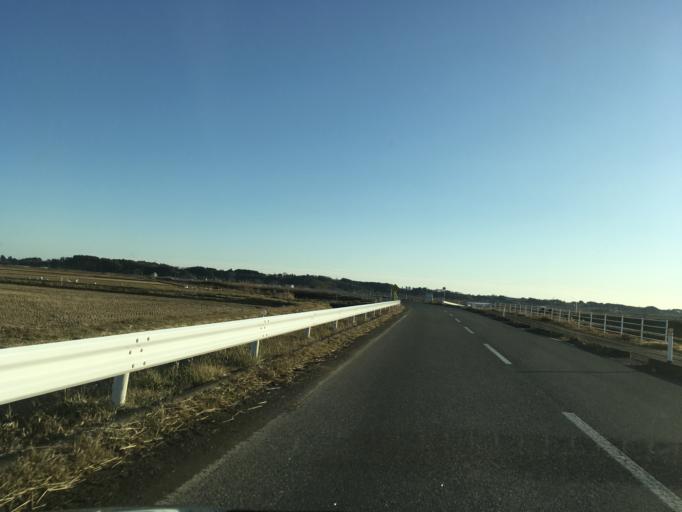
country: JP
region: Iwate
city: Ichinoseki
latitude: 38.7320
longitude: 141.1241
